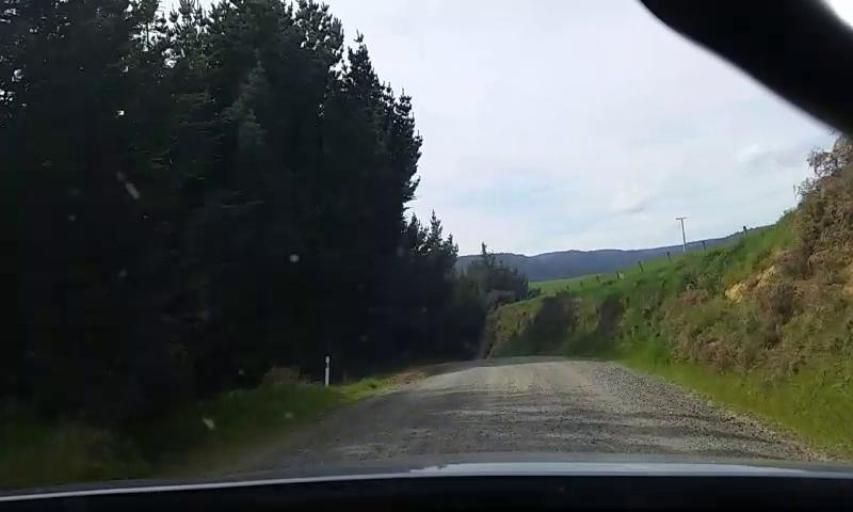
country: NZ
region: Otago
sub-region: Clutha District
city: Papatowai
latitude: -46.6280
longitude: 168.9899
